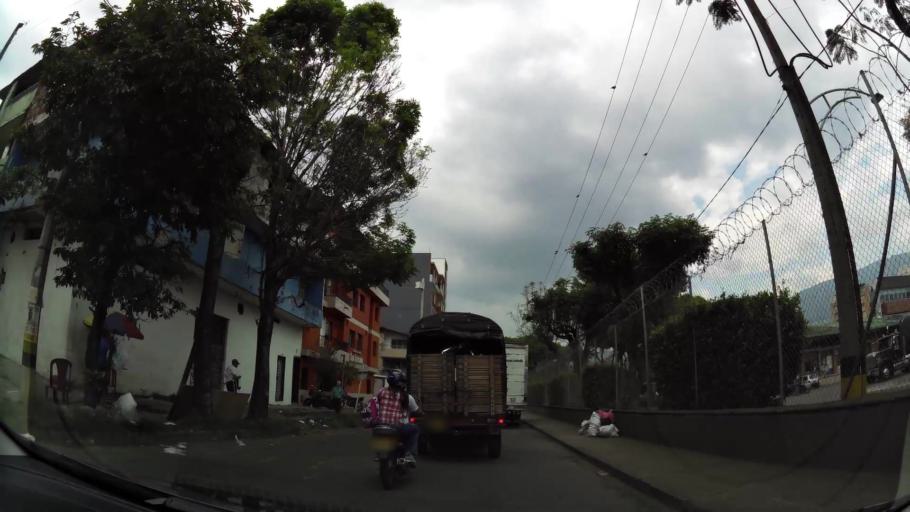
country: CO
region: Antioquia
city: Itagui
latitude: 6.1889
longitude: -75.5922
